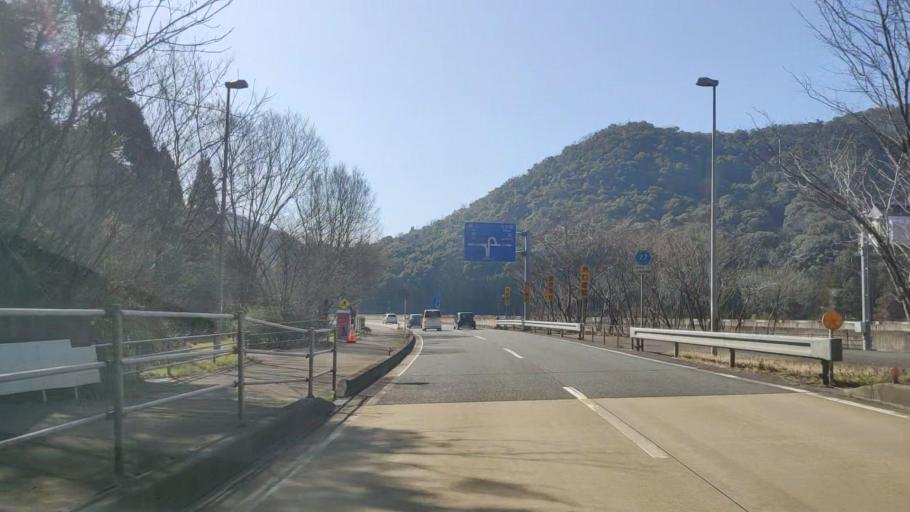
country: JP
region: Gifu
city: Gifu-shi
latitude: 35.4318
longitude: 136.7961
